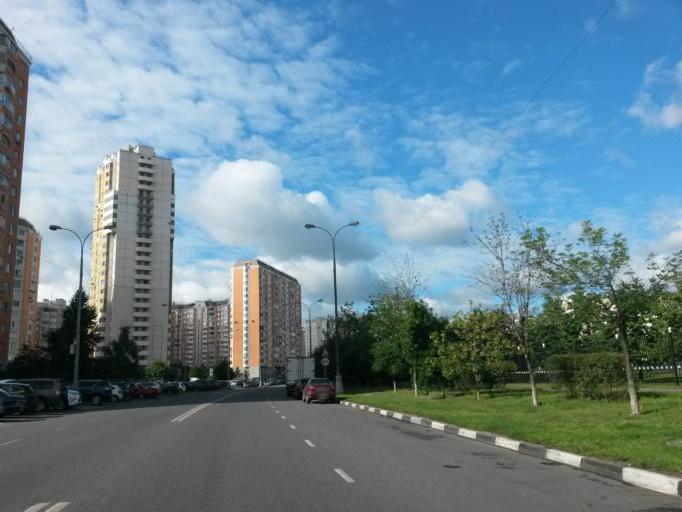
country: RU
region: Moscow
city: Brateyevo
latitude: 55.6612
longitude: 37.7724
